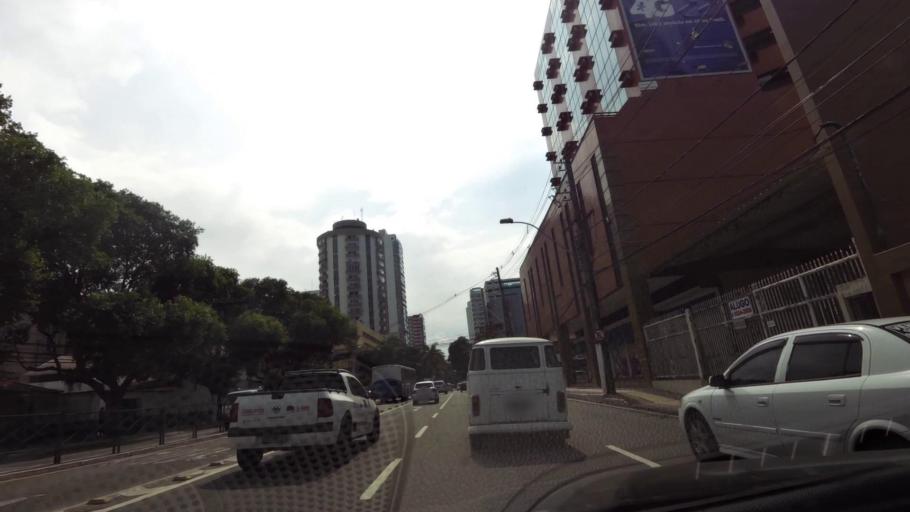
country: BR
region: Espirito Santo
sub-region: Vila Velha
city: Vila Velha
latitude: -20.3093
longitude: -40.2960
